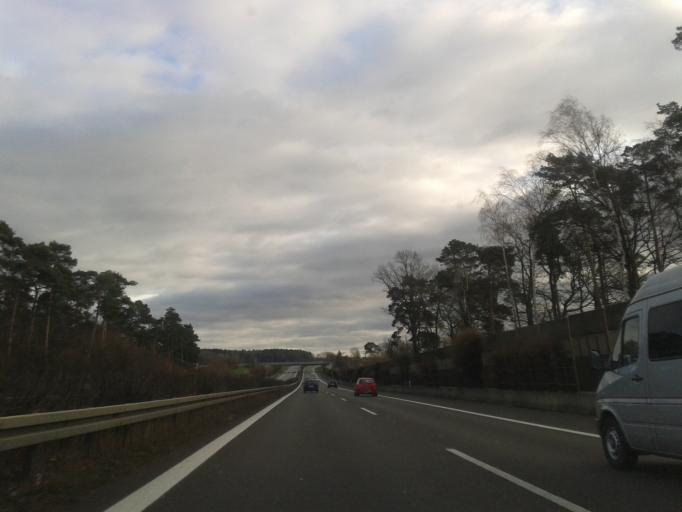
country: DE
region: Saxony
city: Wachau
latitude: 51.1707
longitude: 13.9007
